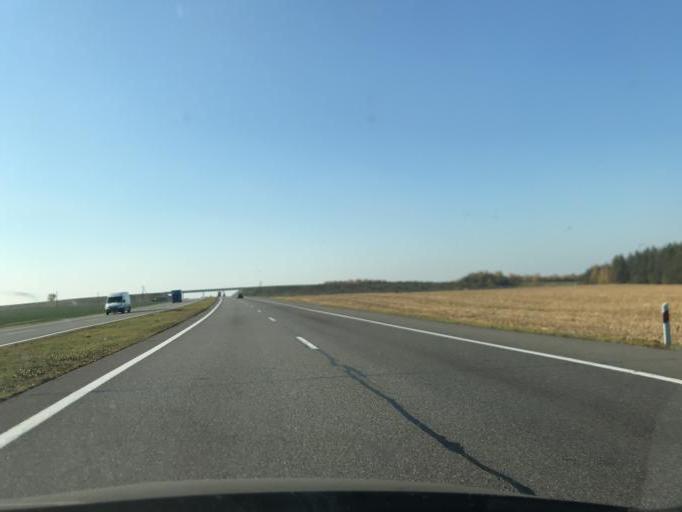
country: BY
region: Minsk
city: Stowbtsy
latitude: 53.5356
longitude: 26.8120
